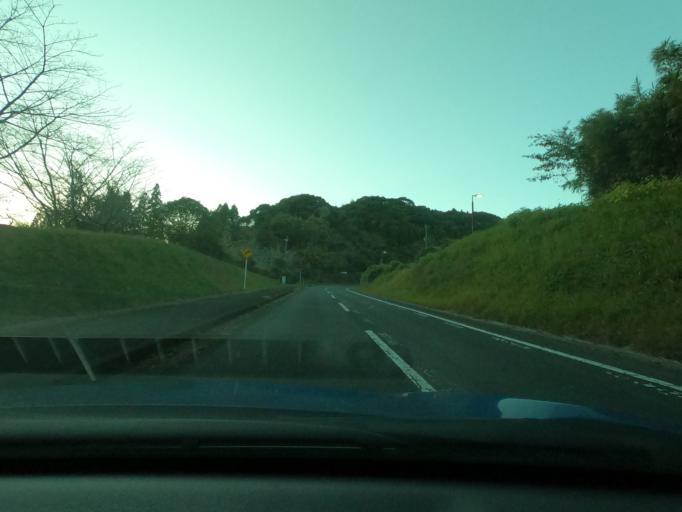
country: JP
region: Kagoshima
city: Satsumasendai
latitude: 31.8102
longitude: 130.4849
